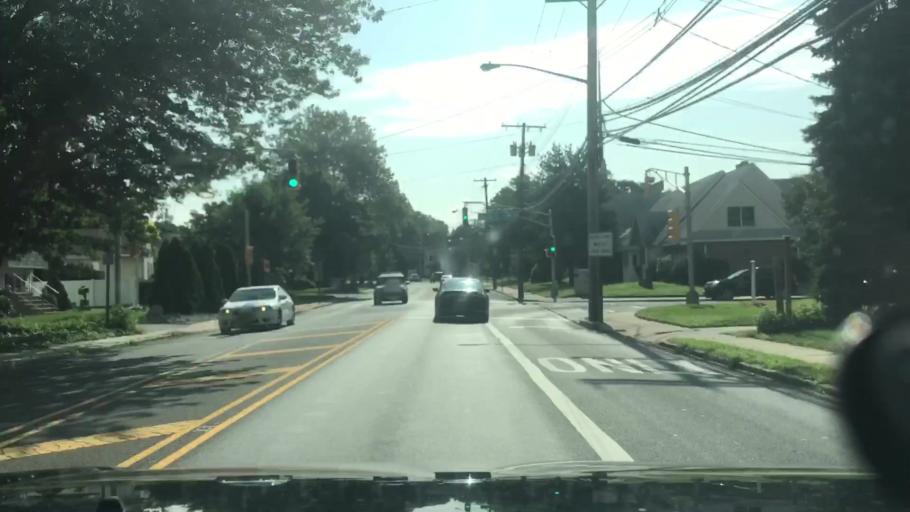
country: US
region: New Jersey
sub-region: Monmouth County
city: West Long Branch
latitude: 40.2990
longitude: -74.0177
